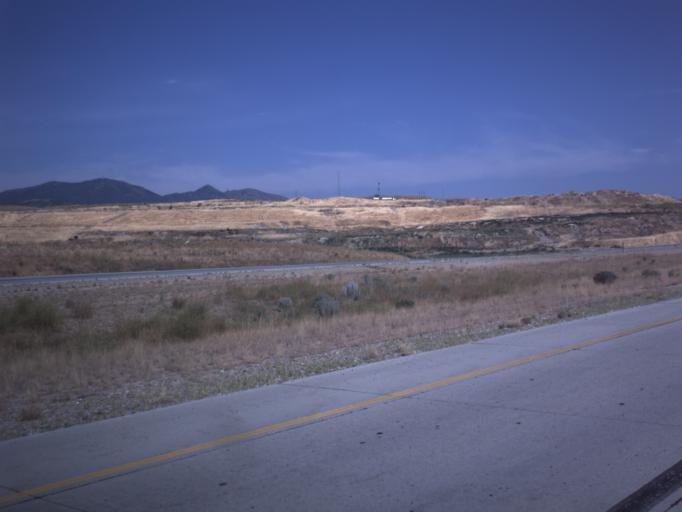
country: US
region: Utah
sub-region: Salt Lake County
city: Oquirrh
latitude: 40.6199
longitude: -112.0425
